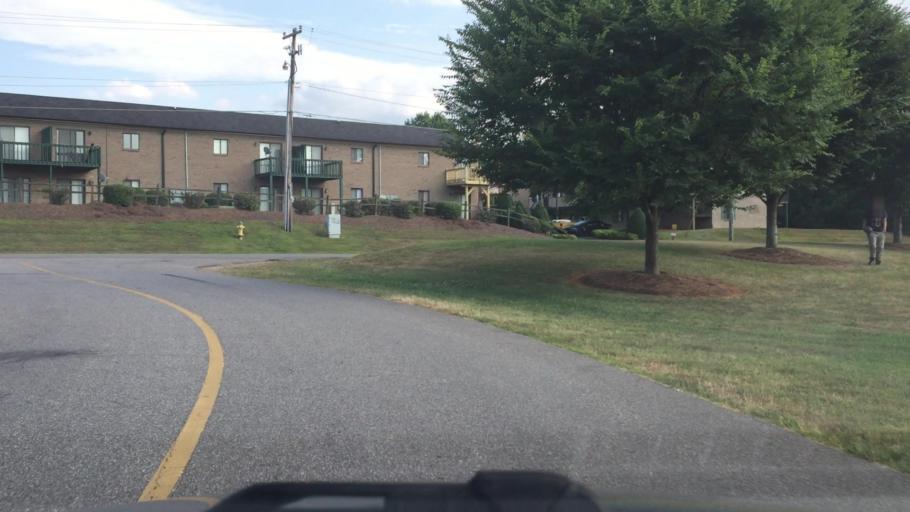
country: US
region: North Carolina
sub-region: Iredell County
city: Statesville
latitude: 35.8009
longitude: -80.8527
